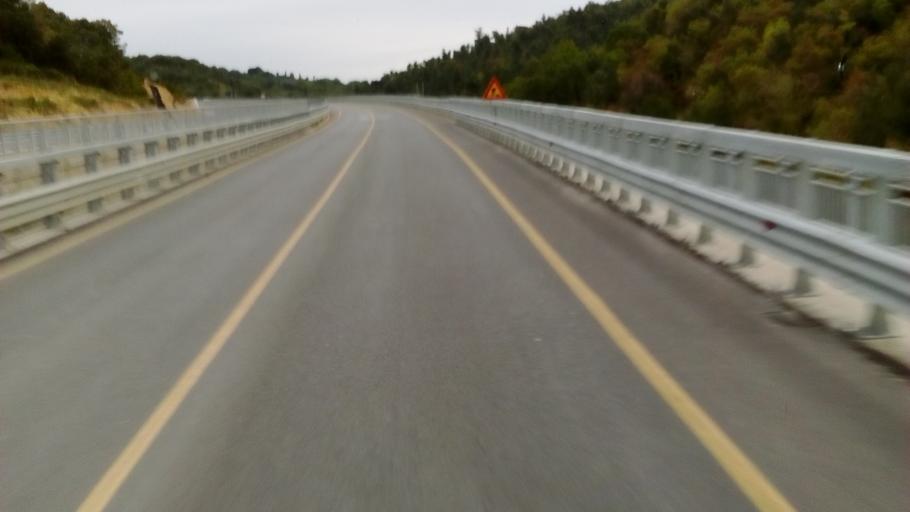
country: IT
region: Tuscany
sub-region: Provincia di Grosseto
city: Civitella Marittima
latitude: 43.0395
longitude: 11.2812
